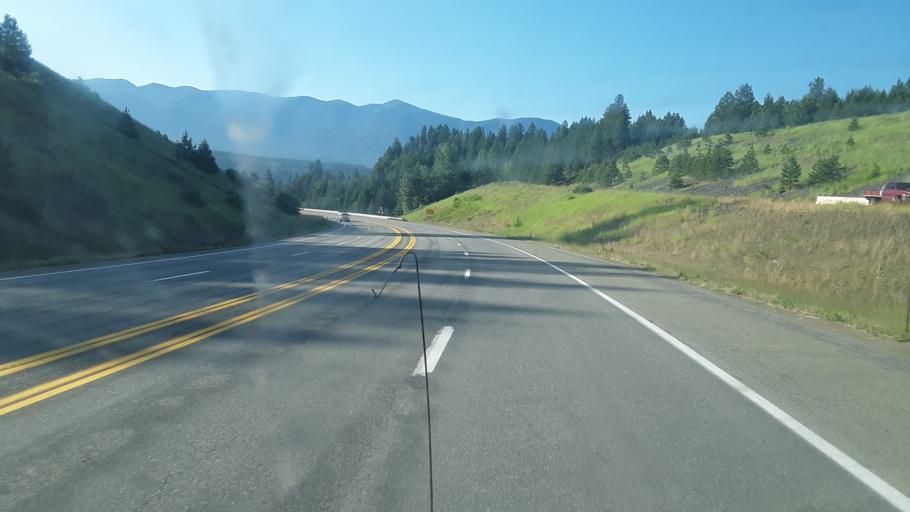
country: US
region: Idaho
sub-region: Boundary County
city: Bonners Ferry
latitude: 48.7175
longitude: -116.3105
